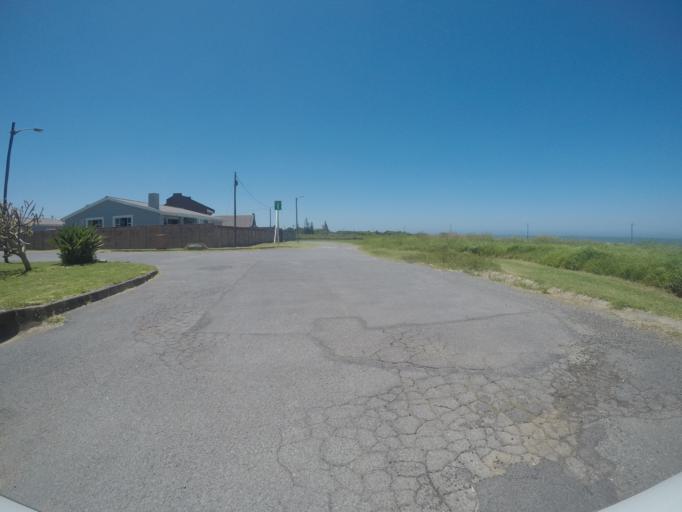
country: ZA
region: Eastern Cape
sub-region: Buffalo City Metropolitan Municipality
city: East London
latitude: -32.9526
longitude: 28.0110
